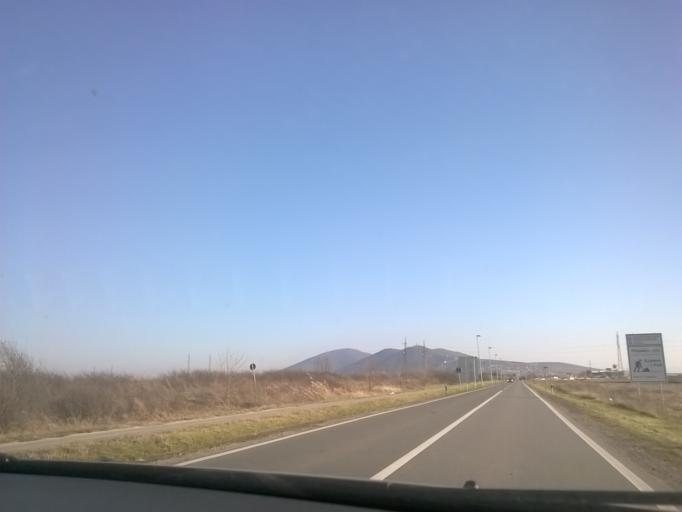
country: RS
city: Pavlis
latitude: 45.1122
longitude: 21.2638
